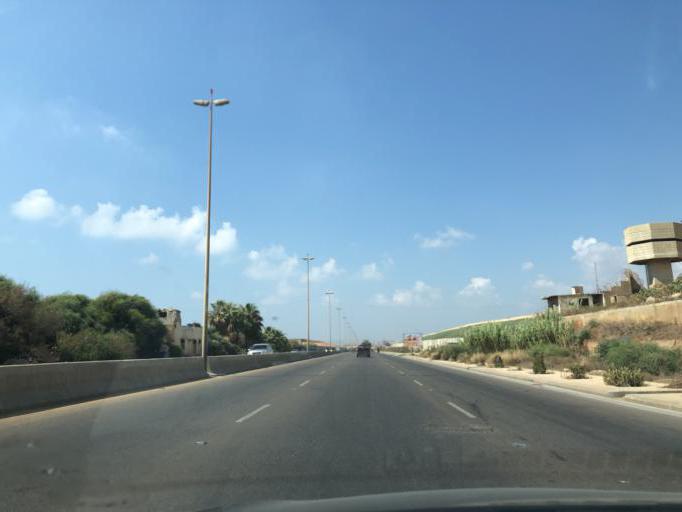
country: LB
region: Mont-Liban
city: Baabda
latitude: 33.8080
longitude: 35.4819
